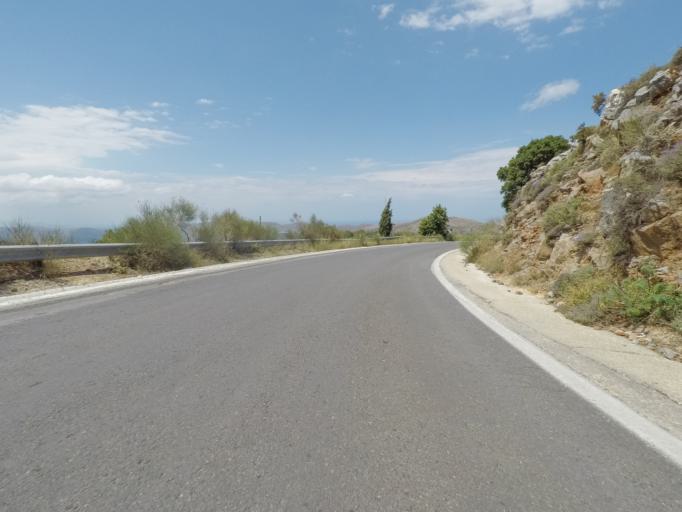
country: GR
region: Crete
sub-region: Nomos Irakleiou
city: Mokhos
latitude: 35.2167
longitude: 25.4588
